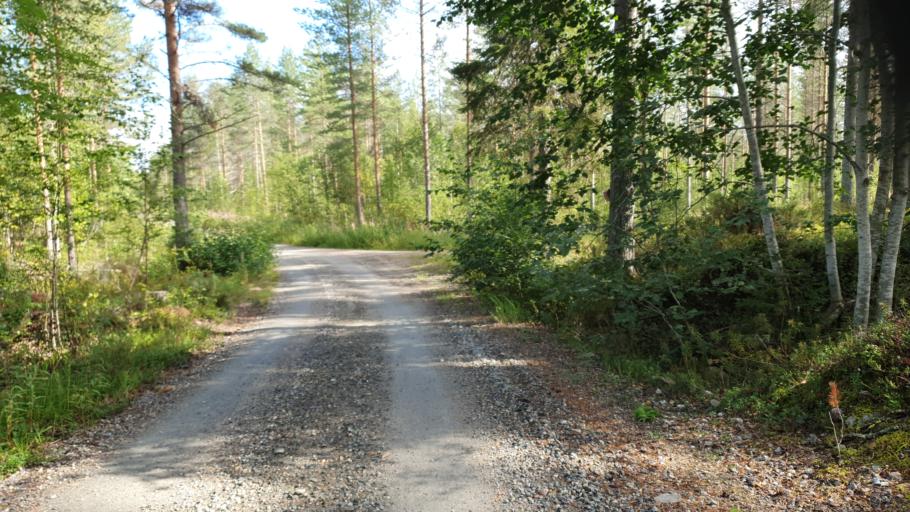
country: FI
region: Kainuu
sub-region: Kehys-Kainuu
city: Kuhmo
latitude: 64.1300
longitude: 29.3482
